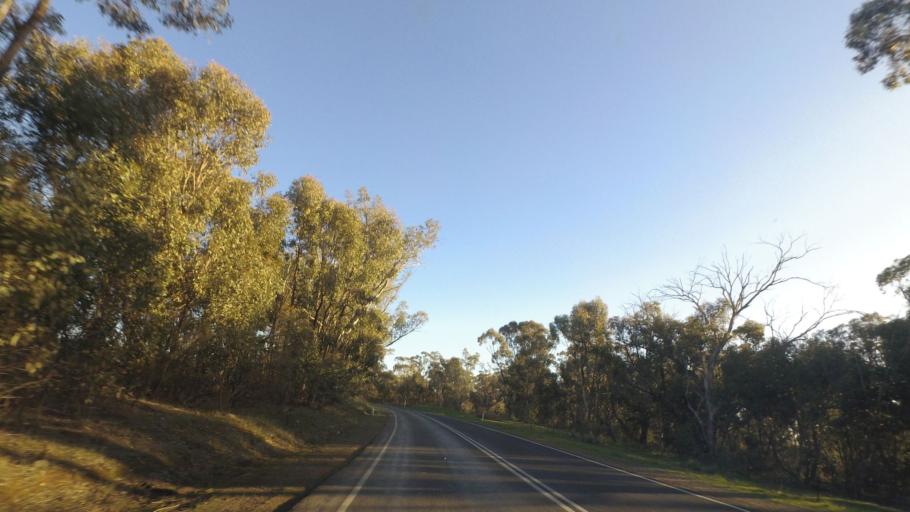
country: AU
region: Victoria
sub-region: Mount Alexander
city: Castlemaine
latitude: -37.0630
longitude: 144.5145
